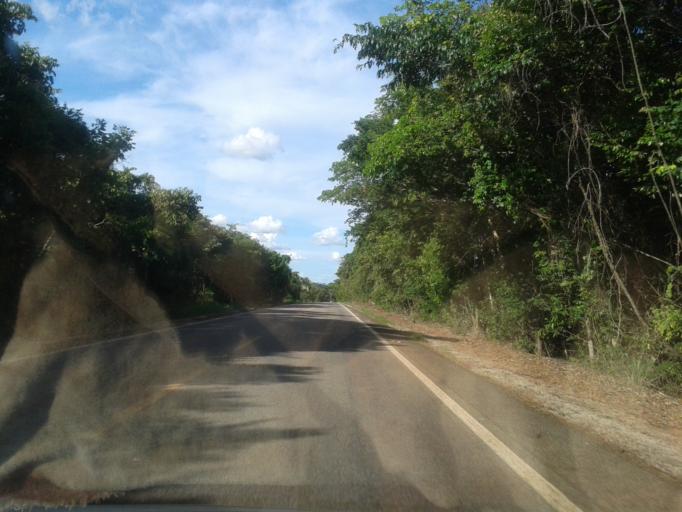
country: BR
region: Goias
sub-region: Mozarlandia
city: Mozarlandia
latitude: -14.4366
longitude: -50.4569
